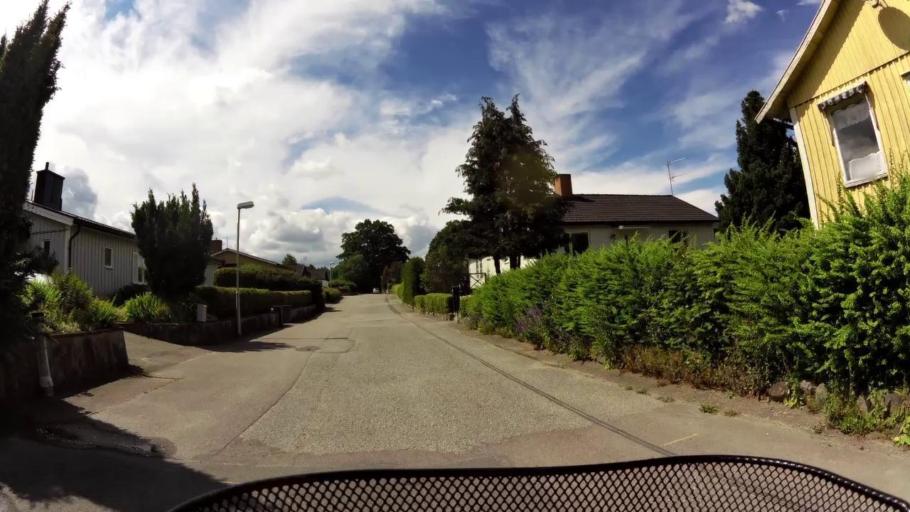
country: SE
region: OEstergoetland
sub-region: Linkopings Kommun
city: Malmslatt
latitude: 58.4190
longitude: 15.5230
